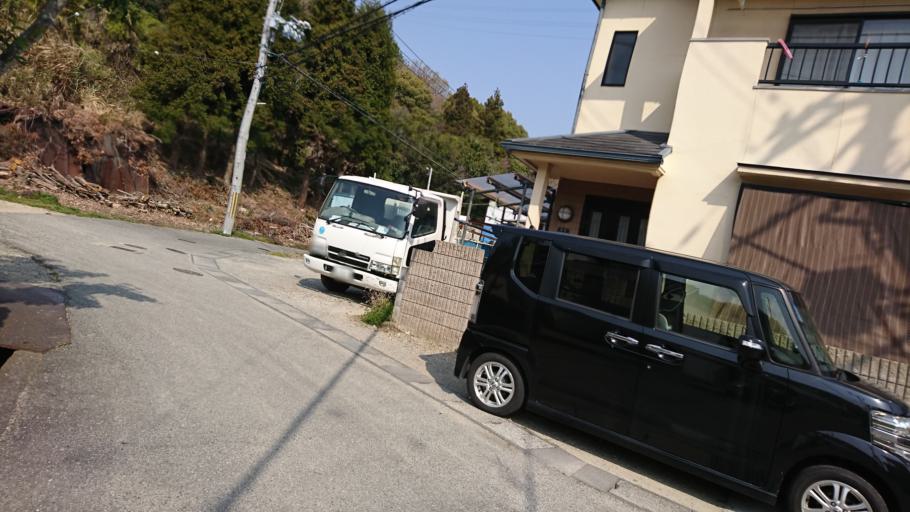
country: JP
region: Hyogo
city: Shirahamacho-usazakiminami
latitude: 34.7863
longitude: 134.7656
